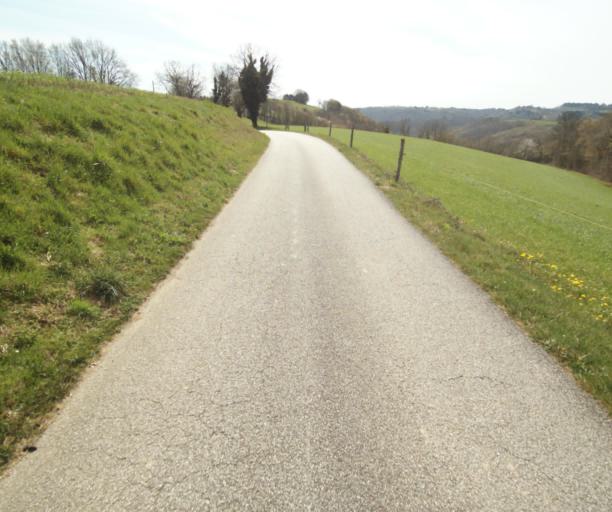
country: FR
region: Limousin
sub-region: Departement de la Correze
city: Naves
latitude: 45.3560
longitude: 1.7969
